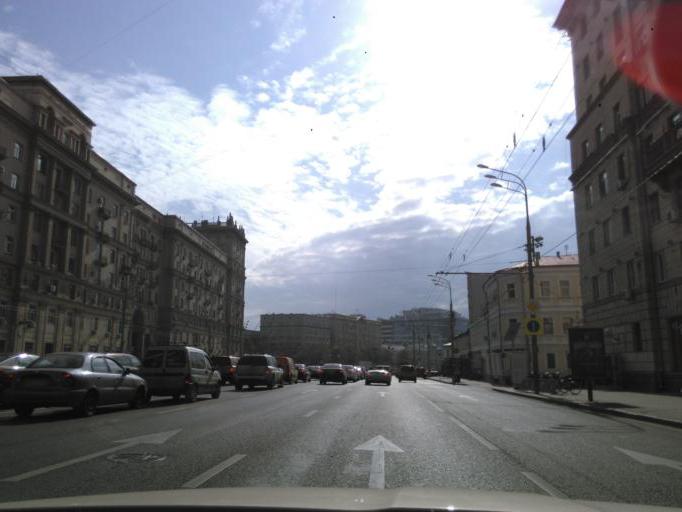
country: RU
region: Moscow
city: Taganskiy
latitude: 55.7653
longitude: 37.6544
